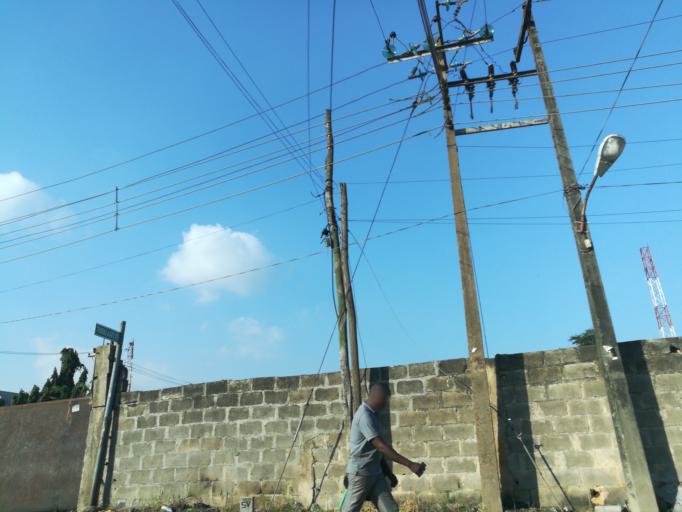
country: NG
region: Lagos
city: Ojota
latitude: 6.5874
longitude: 3.3642
